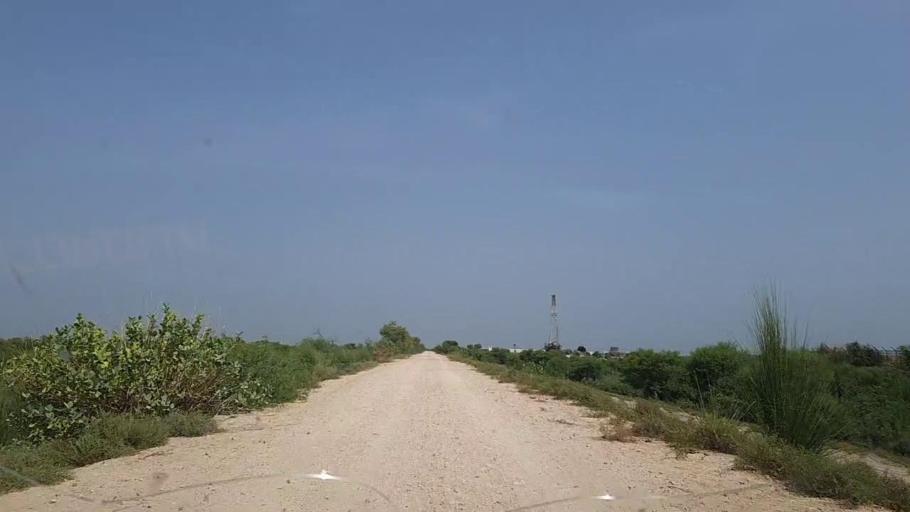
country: PK
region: Sindh
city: Ghotki
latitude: 28.1176
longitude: 69.3812
